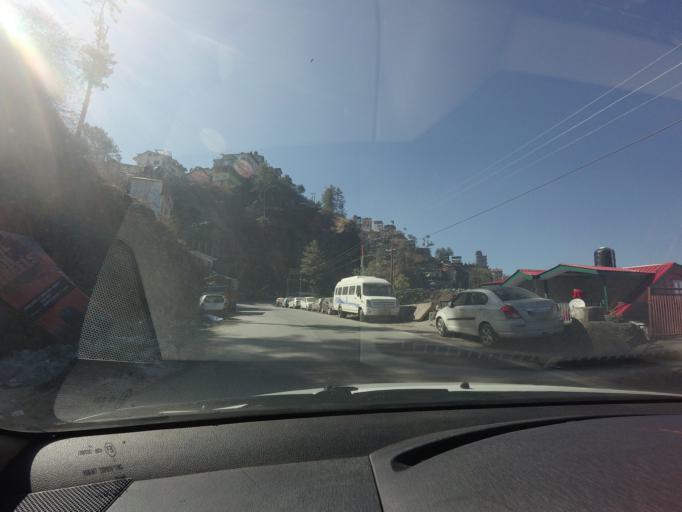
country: IN
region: Himachal Pradesh
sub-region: Shimla
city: Shimla
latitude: 31.1085
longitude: 77.2102
